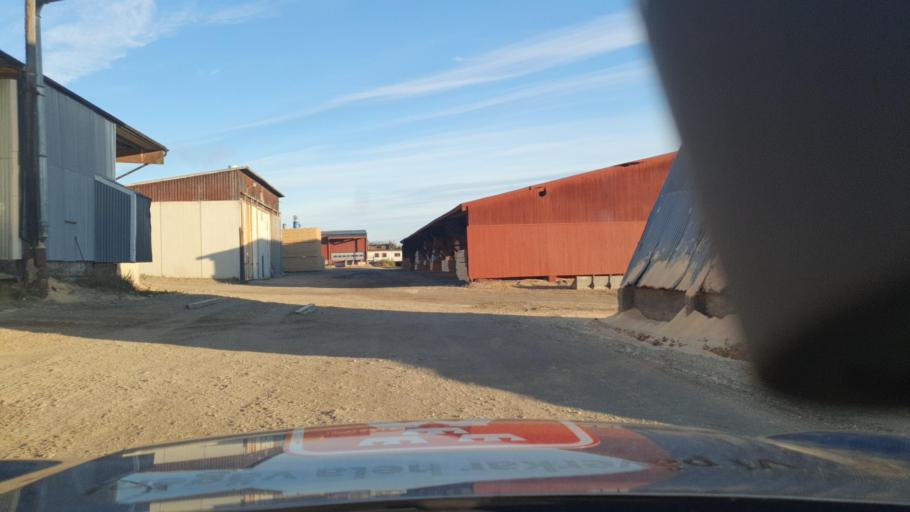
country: SE
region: Norrbotten
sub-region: Pajala Kommun
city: Pajala
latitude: 67.1905
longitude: 22.5954
